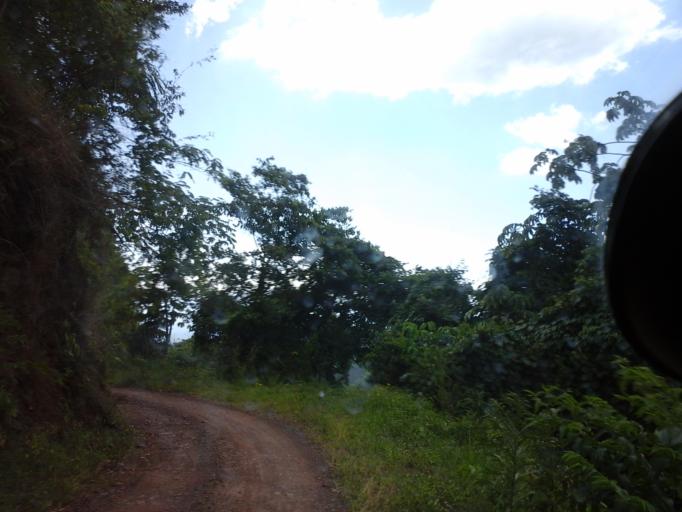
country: CO
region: Cesar
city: San Diego
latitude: 10.2700
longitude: -73.0823
